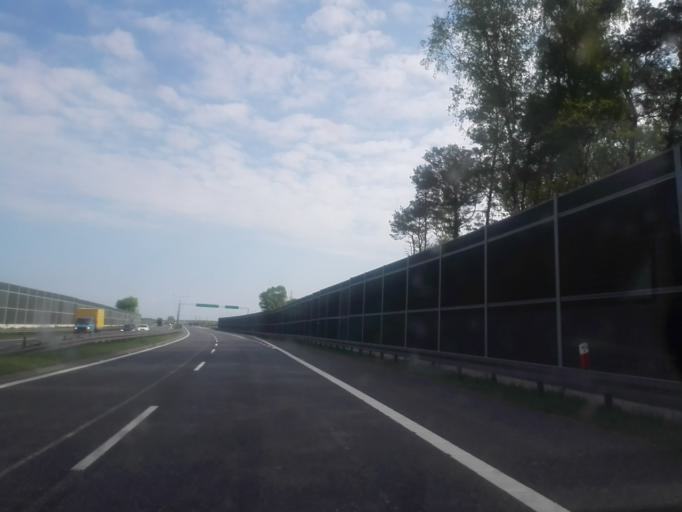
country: PL
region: Masovian Voivodeship
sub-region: Powiat zyrardowski
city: Mszczonow
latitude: 51.9322
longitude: 20.4734
